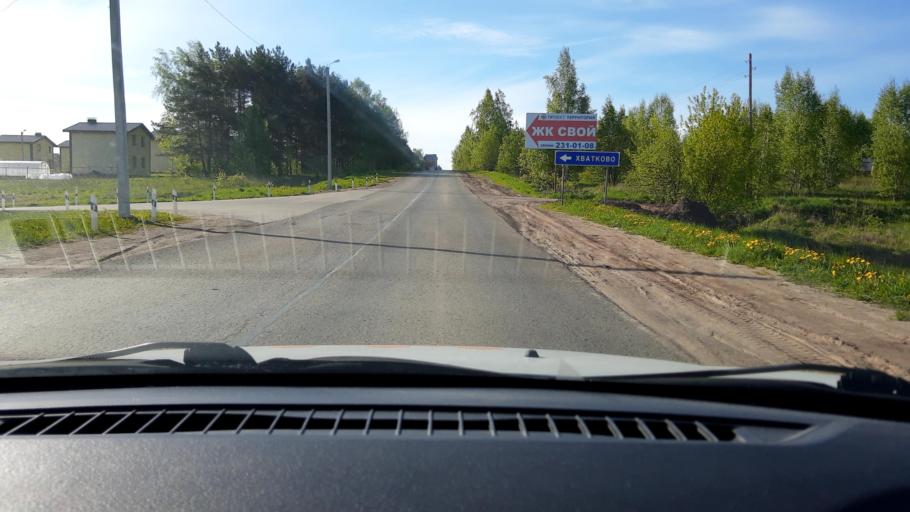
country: RU
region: Nizjnij Novgorod
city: Burevestnik
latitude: 56.1676
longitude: 43.7672
